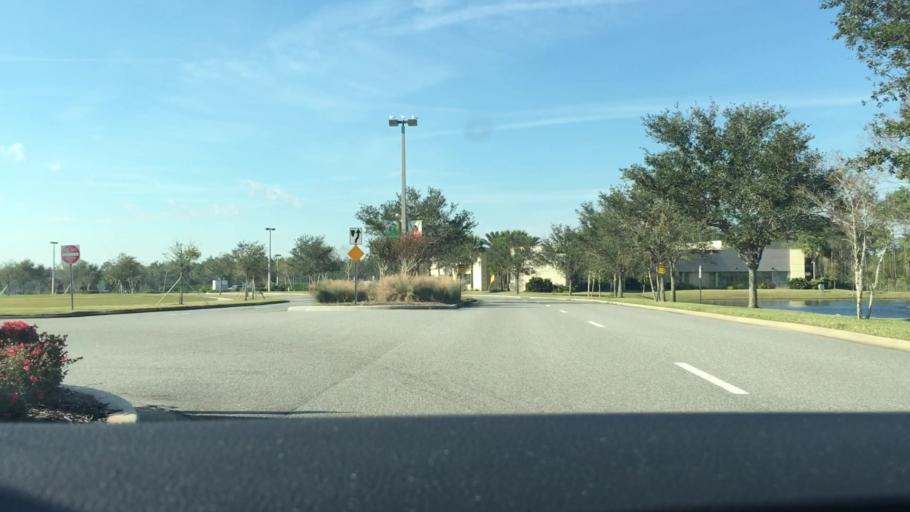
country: US
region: Florida
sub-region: Volusia County
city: Ormond Beach
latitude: 29.2456
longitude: -81.1086
